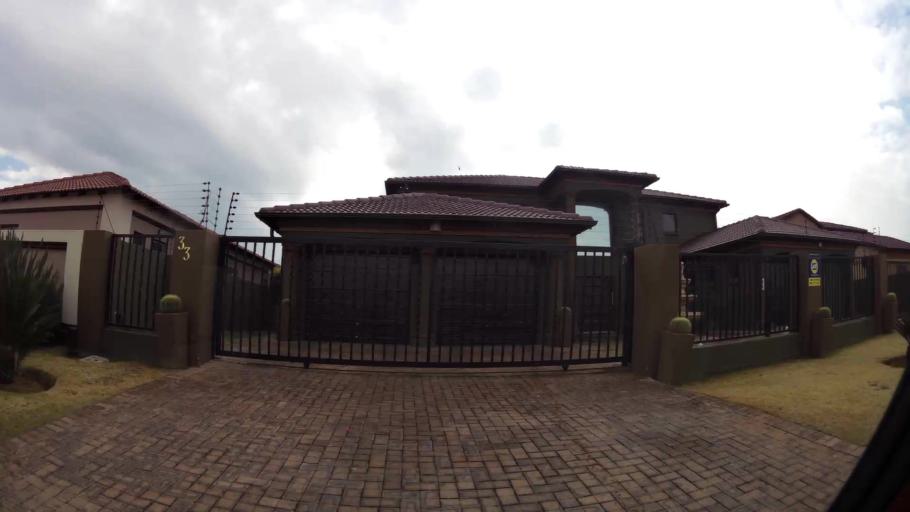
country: ZA
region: Gauteng
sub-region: Sedibeng District Municipality
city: Vanderbijlpark
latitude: -26.7240
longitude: 27.8659
